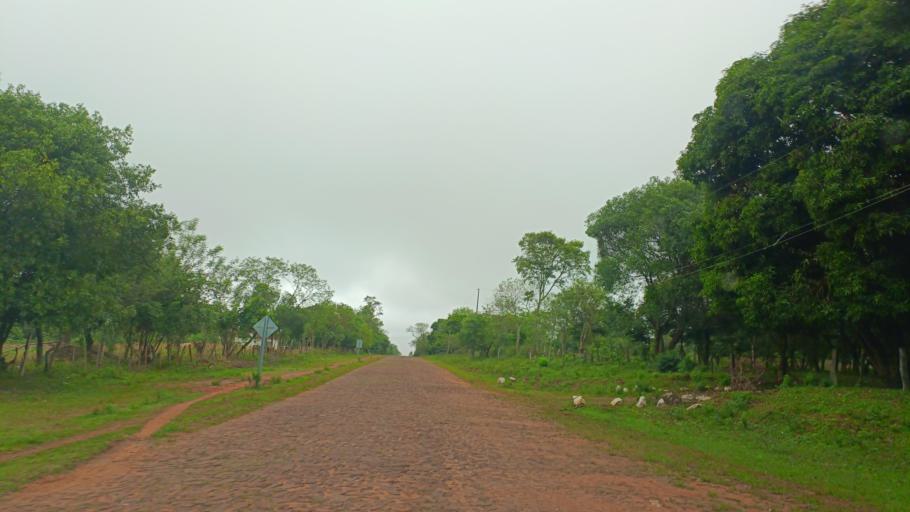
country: PY
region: Misiones
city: Santa Maria
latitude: -26.8633
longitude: -57.0107
